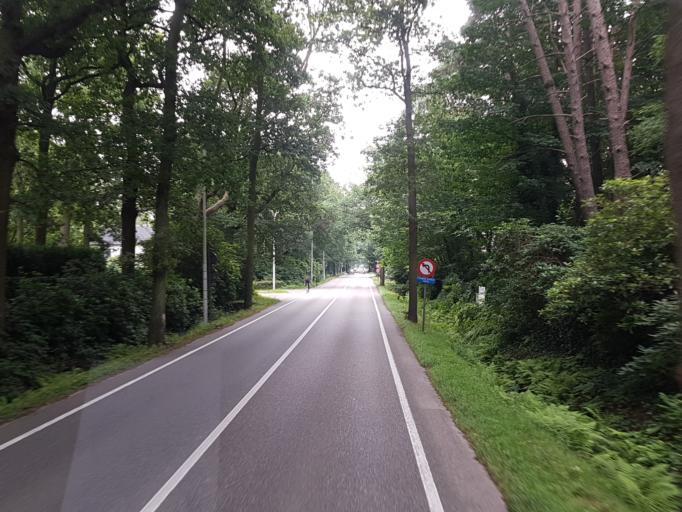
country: BE
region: Flanders
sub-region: Provincie Antwerpen
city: Schoten
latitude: 51.2684
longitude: 4.5326
